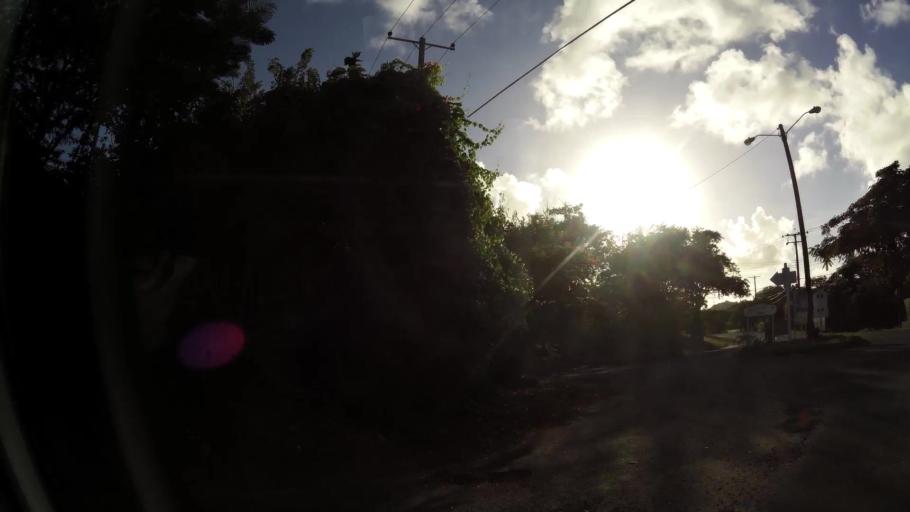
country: LC
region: Gros-Islet
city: Gros Islet
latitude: 14.0967
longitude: -60.9438
